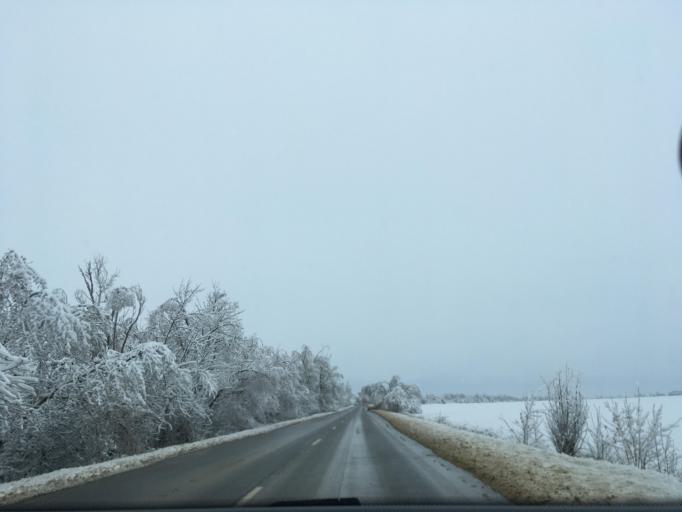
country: RU
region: Voronezj
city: Ol'khovatka
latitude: 50.2060
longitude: 39.2488
